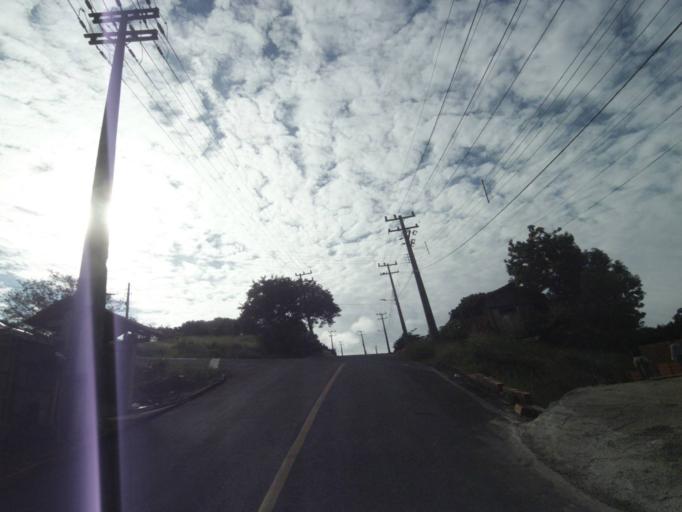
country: BR
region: Parana
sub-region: Telemaco Borba
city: Telemaco Borba
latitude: -24.3395
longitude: -50.6145
